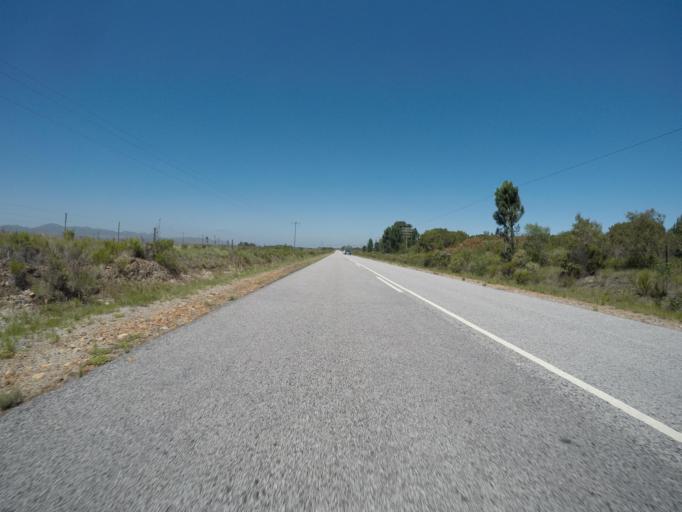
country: ZA
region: Eastern Cape
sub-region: Cacadu District Municipality
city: Kareedouw
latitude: -33.9815
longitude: 24.5067
